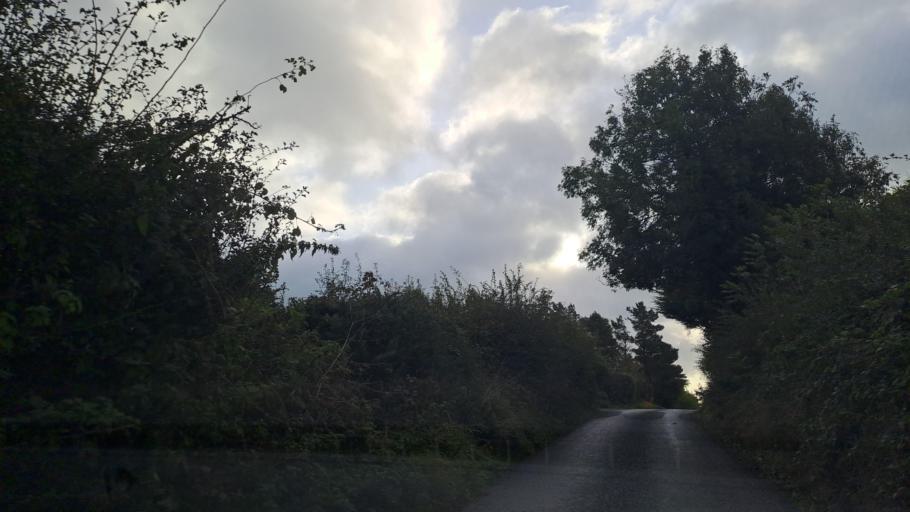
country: IE
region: Ulster
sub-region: An Cabhan
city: Kingscourt
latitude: 53.9573
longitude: -6.8030
